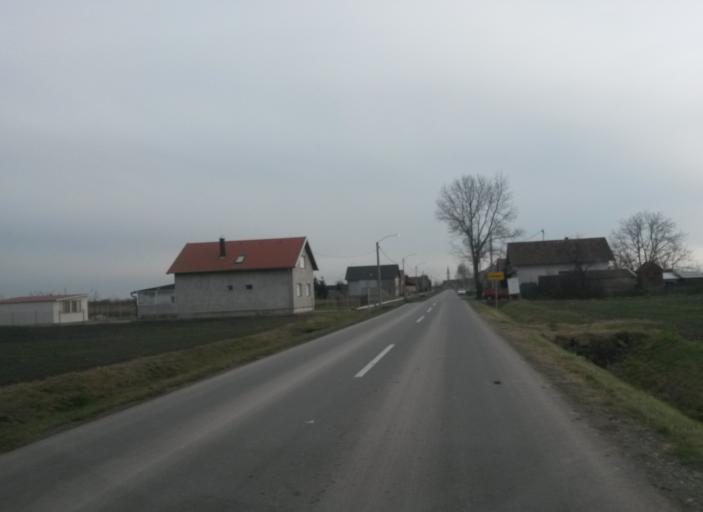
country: HR
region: Osjecko-Baranjska
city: Antunovac
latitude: 45.4915
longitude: 18.6259
